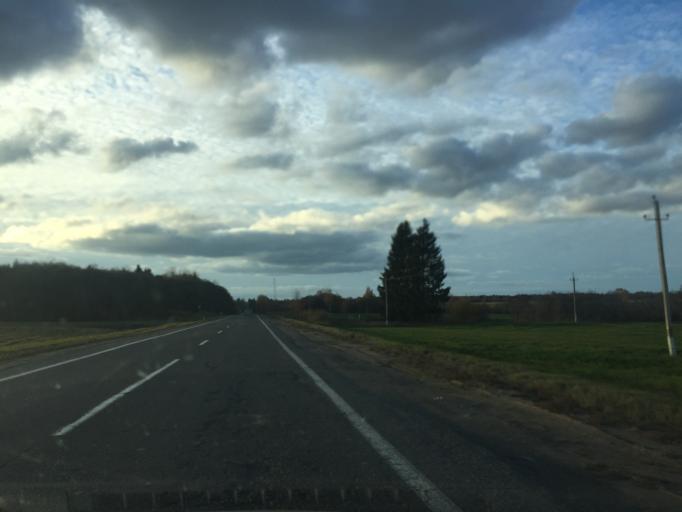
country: BY
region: Vitebsk
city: Myory
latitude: 55.8168
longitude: 27.6609
